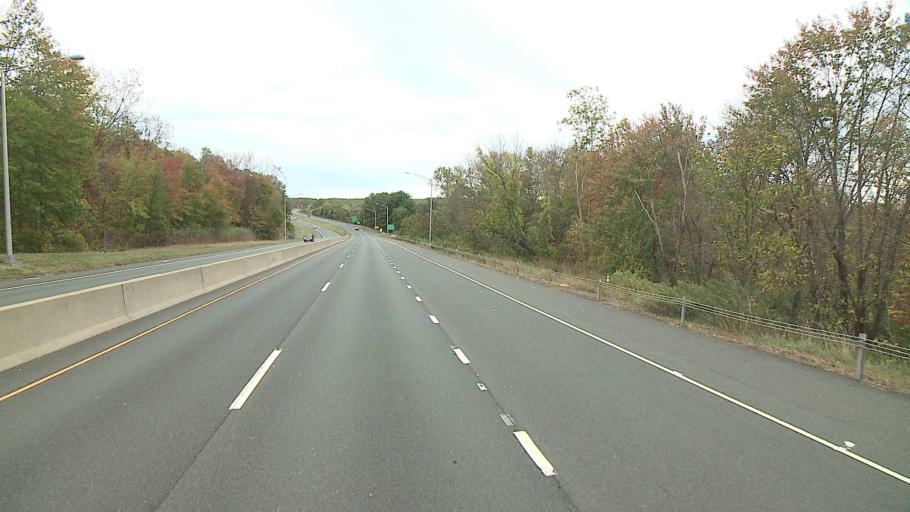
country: US
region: Connecticut
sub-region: Middlesex County
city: Middletown
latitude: 41.5414
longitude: -72.6261
